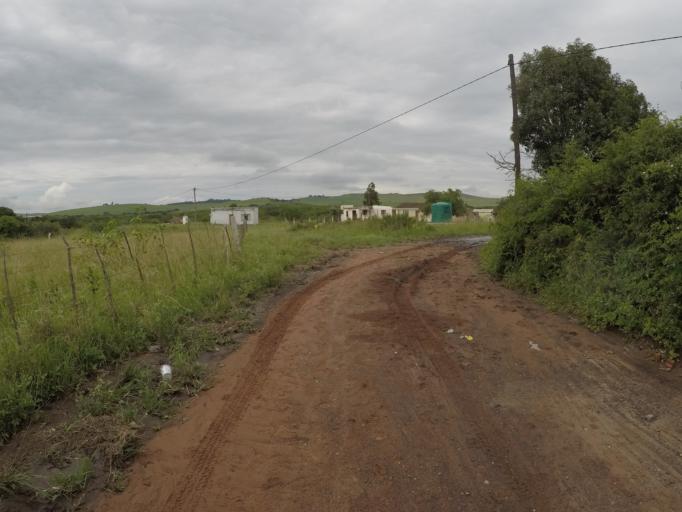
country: ZA
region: KwaZulu-Natal
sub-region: uThungulu District Municipality
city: Empangeni
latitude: -28.7157
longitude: 31.8613
